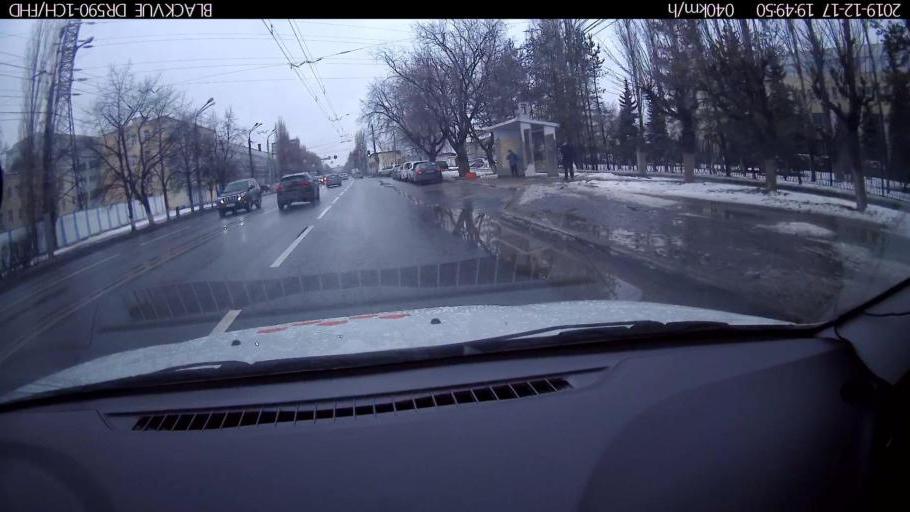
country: RU
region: Nizjnij Novgorod
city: Nizhniy Novgorod
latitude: 56.3303
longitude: 43.9021
